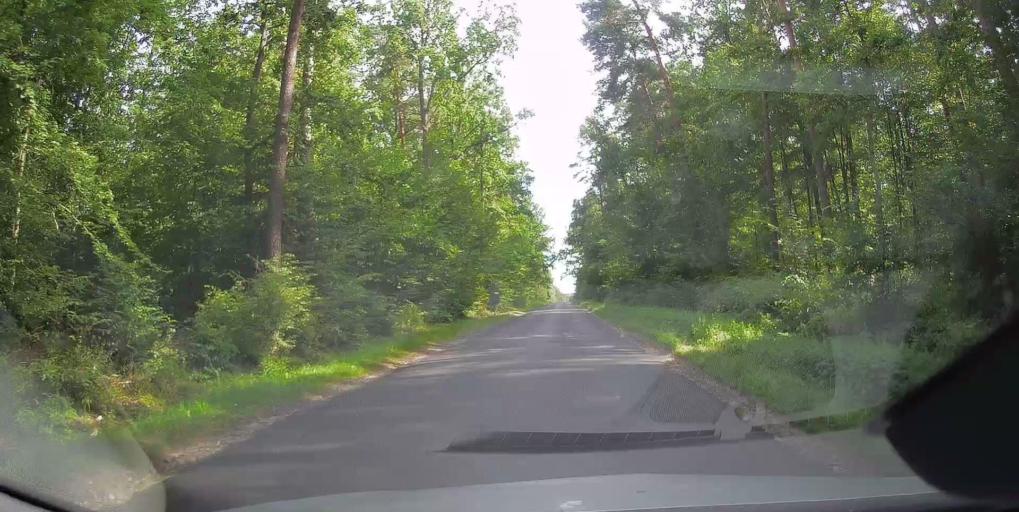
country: PL
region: Lodz Voivodeship
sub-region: Powiat opoczynski
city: Mniszkow
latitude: 51.4346
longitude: 20.0240
